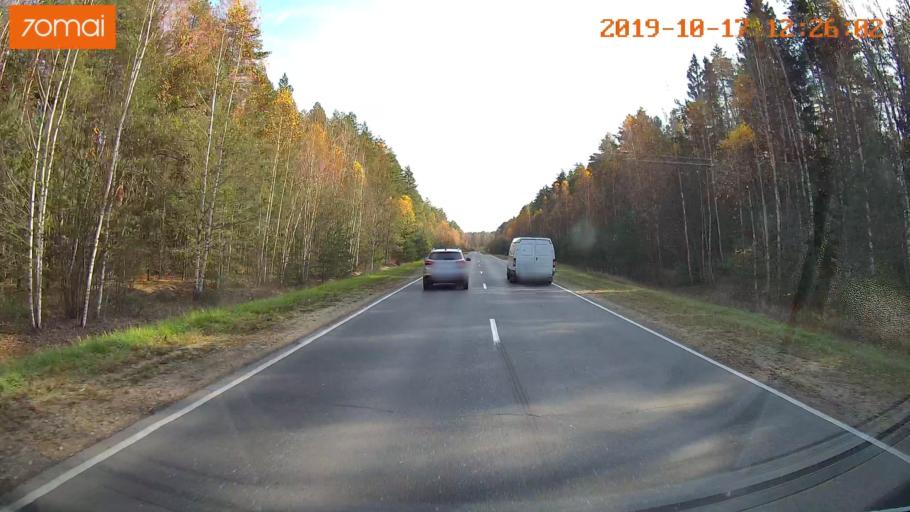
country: RU
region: Rjazan
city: Syntul
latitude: 55.0227
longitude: 41.2478
